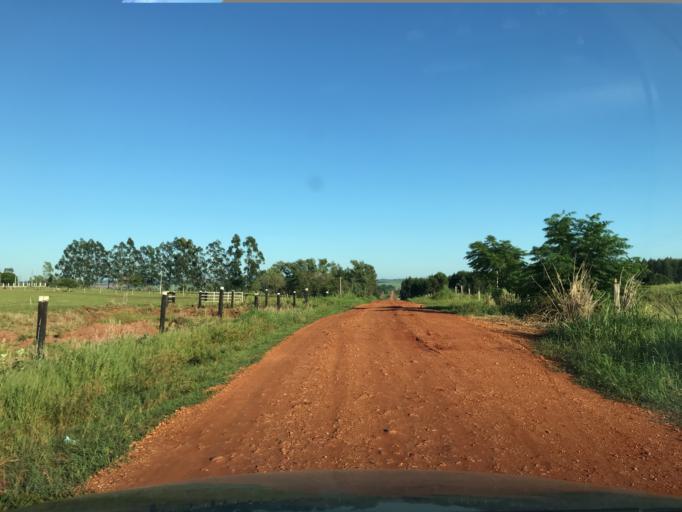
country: BR
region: Parana
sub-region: Ipora
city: Ipora
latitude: -23.9930
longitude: -53.7298
